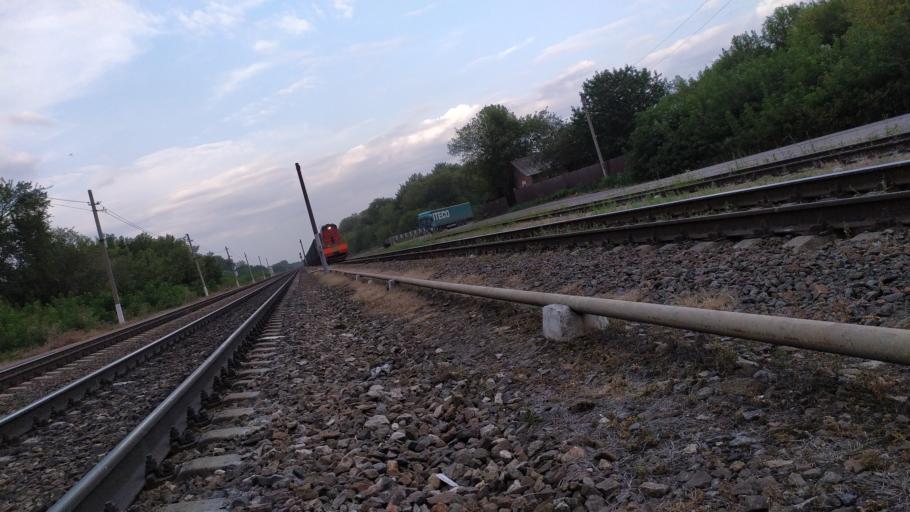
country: RU
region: Kursk
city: Kursk
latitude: 51.6556
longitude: 36.1380
